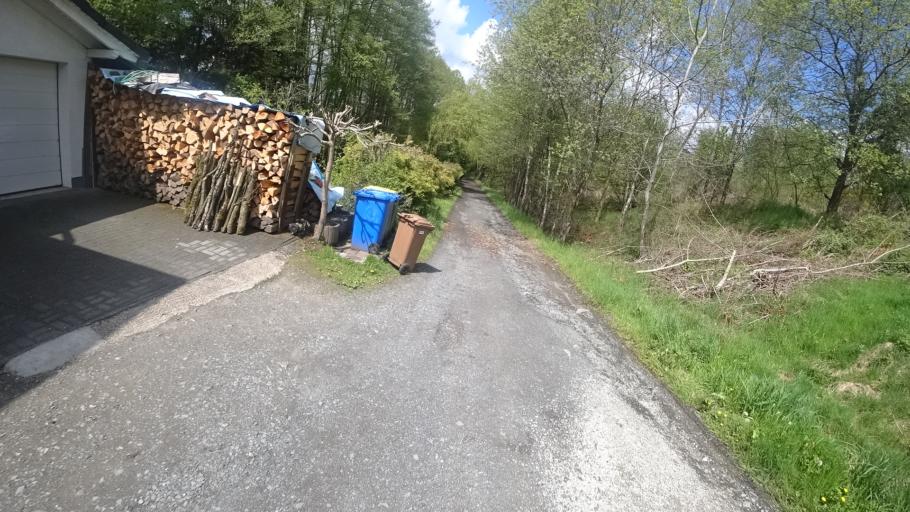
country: DE
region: Rheinland-Pfalz
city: Scheuerfeld
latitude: 50.7834
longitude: 7.8508
